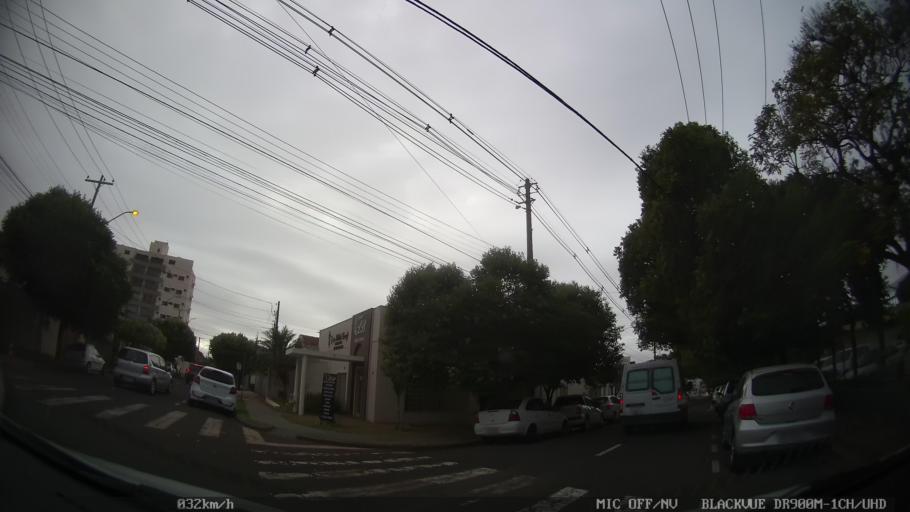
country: BR
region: Sao Paulo
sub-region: Sao Jose Do Rio Preto
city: Sao Jose do Rio Preto
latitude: -20.8278
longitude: -49.3941
